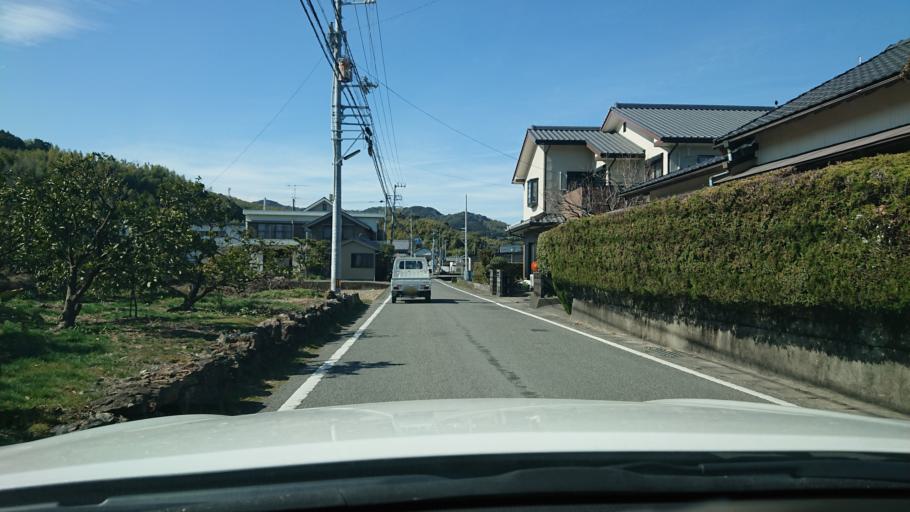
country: JP
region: Tokushima
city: Komatsushimacho
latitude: 33.9796
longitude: 134.5893
